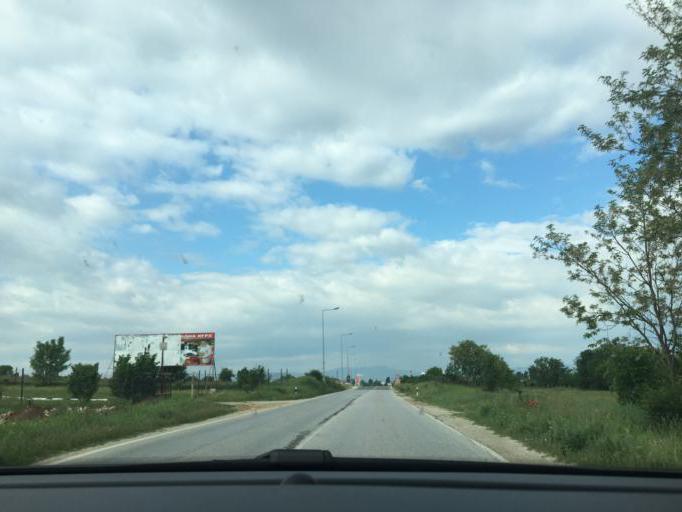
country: MK
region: Prilep
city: Prilep
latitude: 41.3585
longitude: 21.5849
